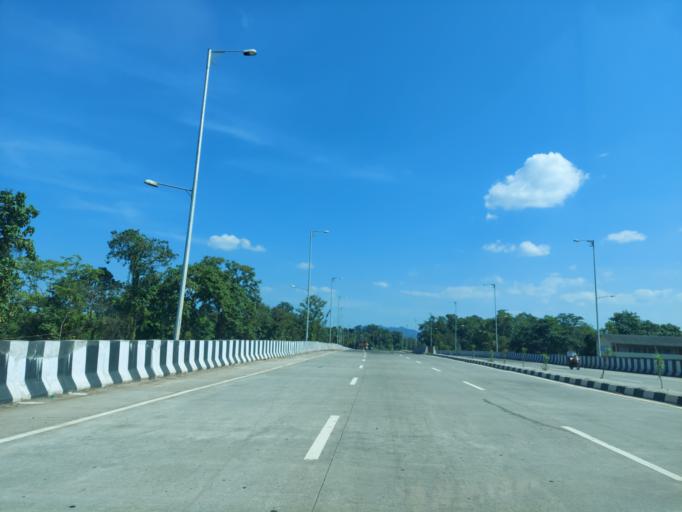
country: IN
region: Maharashtra
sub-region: Sindhudurg
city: Kudal
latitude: 15.9743
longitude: 73.7137
